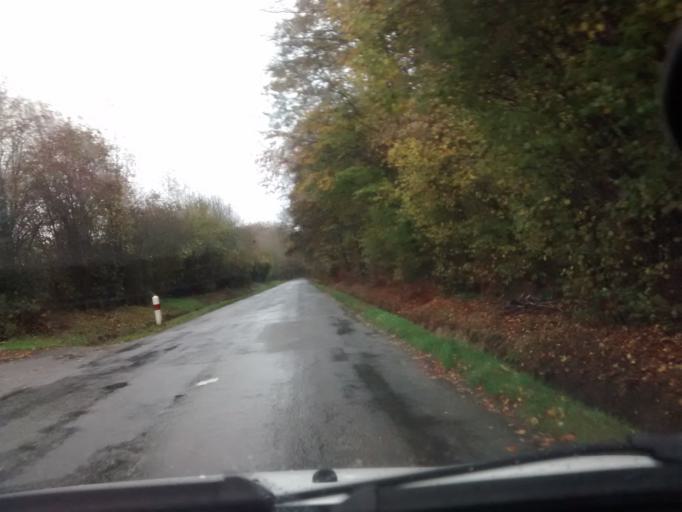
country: FR
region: Brittany
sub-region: Departement d'Ille-et-Vilaine
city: Vern-sur-Seiche
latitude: 48.0669
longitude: -1.6033
